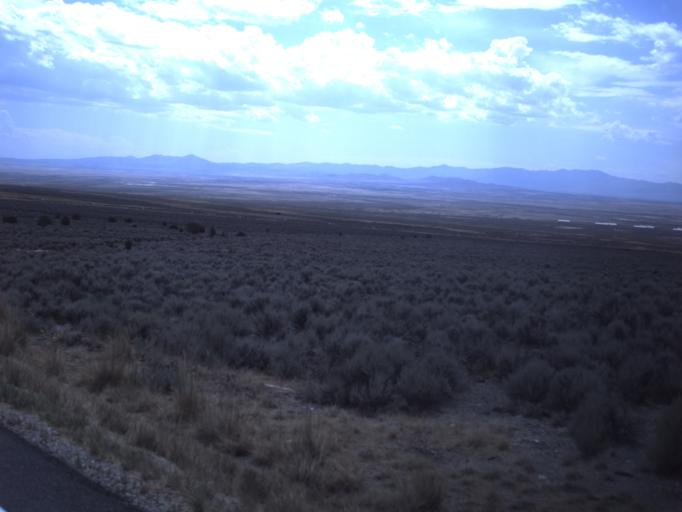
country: US
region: Utah
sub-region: Tooele County
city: Tooele
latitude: 40.3108
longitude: -112.2815
